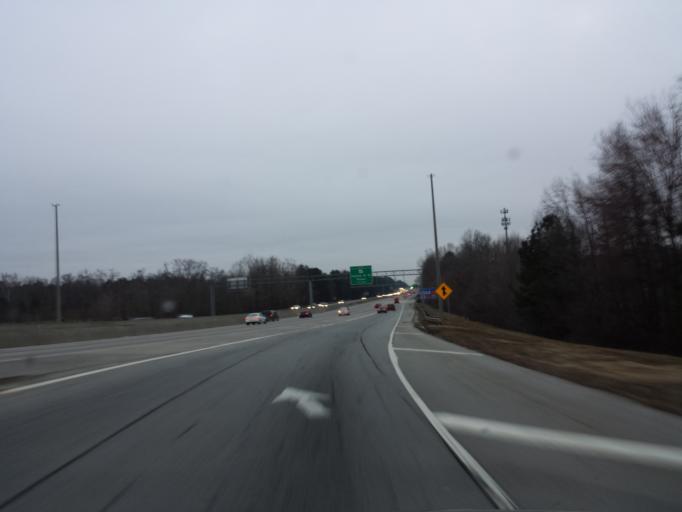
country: US
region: Georgia
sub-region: Fulton County
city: Alpharetta
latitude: 34.0358
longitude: -84.3144
